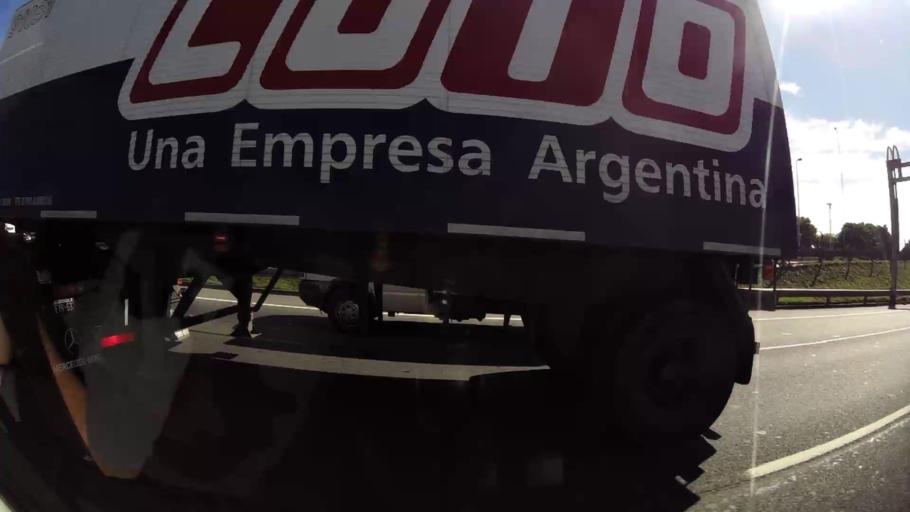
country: AR
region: Buenos Aires
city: Caseros
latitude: -34.6311
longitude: -58.5470
